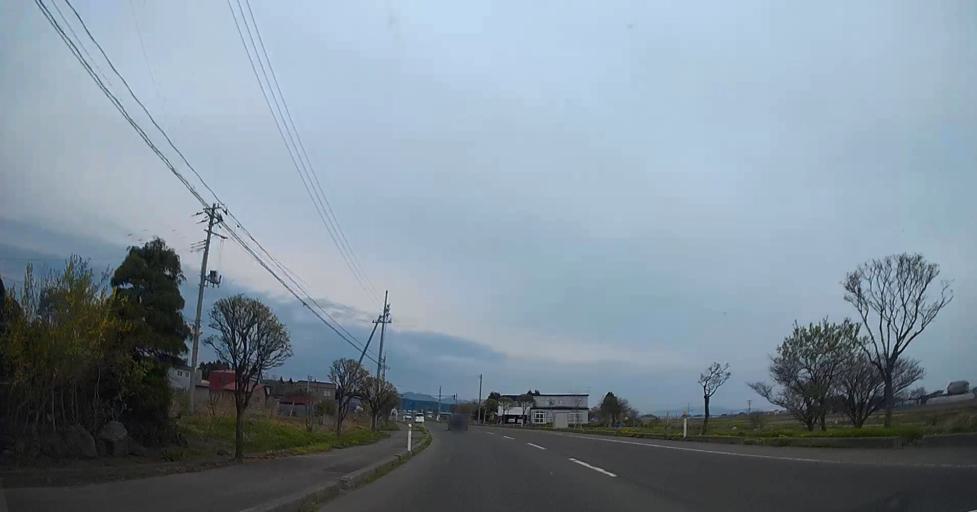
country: JP
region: Aomori
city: Aomori Shi
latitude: 40.8679
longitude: 140.6777
